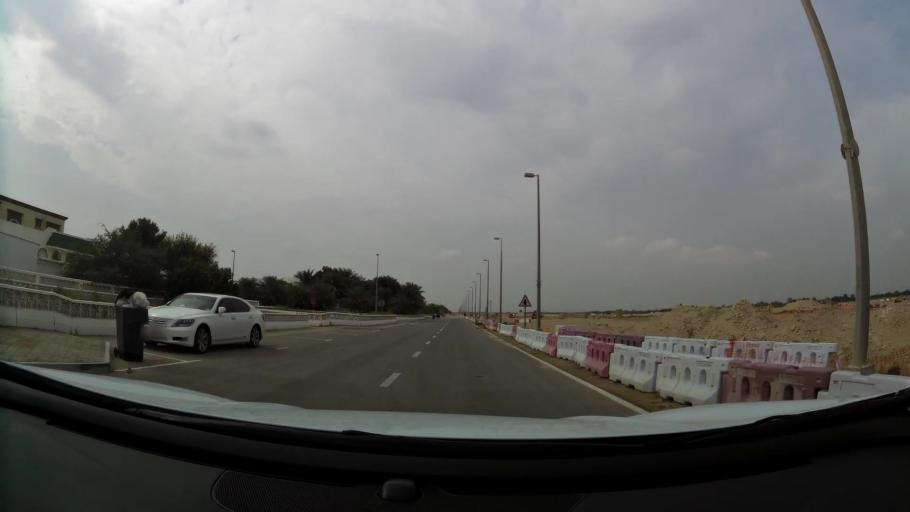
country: AE
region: Abu Dhabi
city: Abu Dhabi
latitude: 24.6360
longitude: 54.7168
